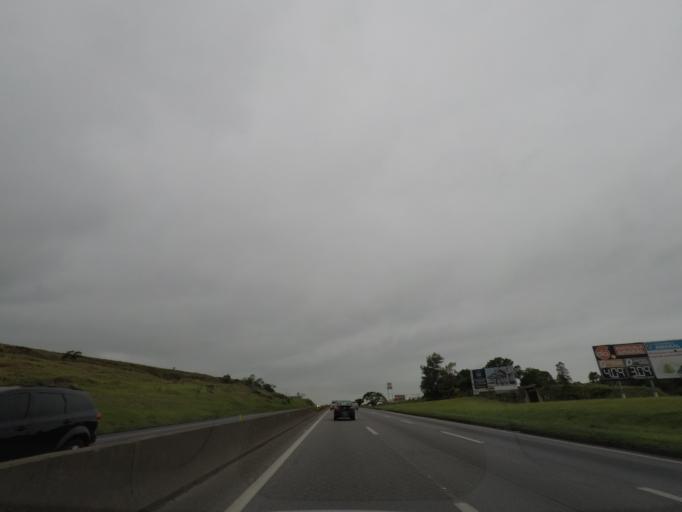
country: BR
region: Sao Paulo
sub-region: Pindamonhangaba
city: Pindamonhangaba
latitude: -22.9921
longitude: -45.4839
